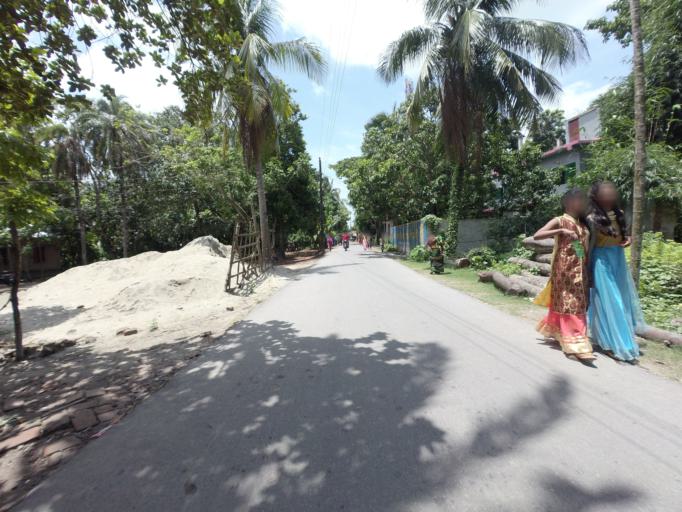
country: BD
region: Khulna
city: Kalia
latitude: 23.0385
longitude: 89.6286
